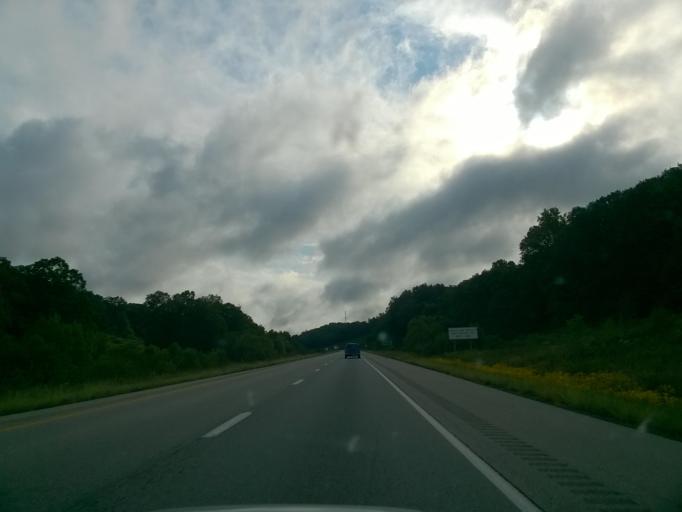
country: US
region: Indiana
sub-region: Dubois County
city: Ferdinand
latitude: 38.2304
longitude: -86.6827
